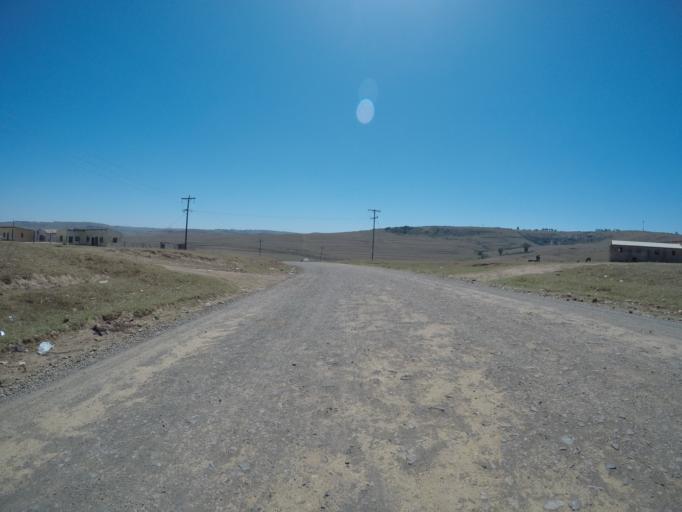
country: ZA
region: Eastern Cape
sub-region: OR Tambo District Municipality
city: Mthatha
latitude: -31.7827
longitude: 28.8060
